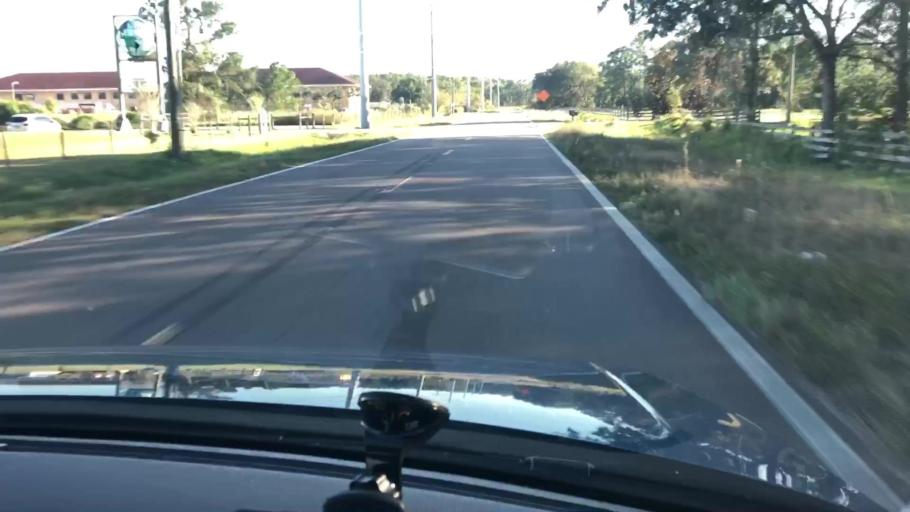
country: US
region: Florida
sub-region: Polk County
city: Polk City
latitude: 28.1489
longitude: -81.8974
